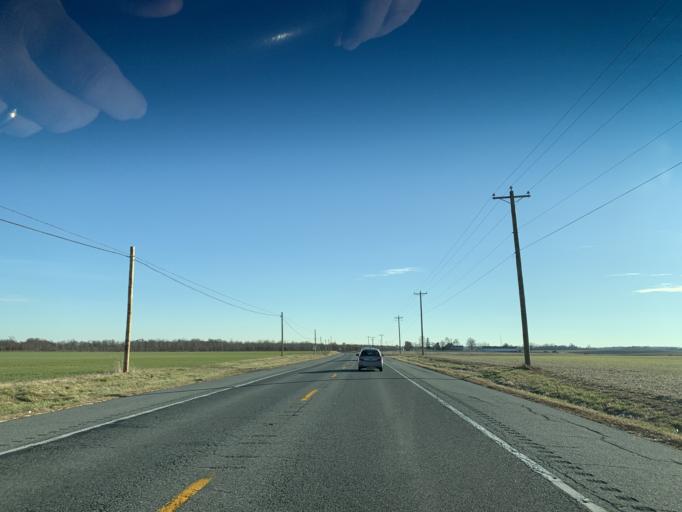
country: US
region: Delaware
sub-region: New Castle County
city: Middletown
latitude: 39.4306
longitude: -75.8609
